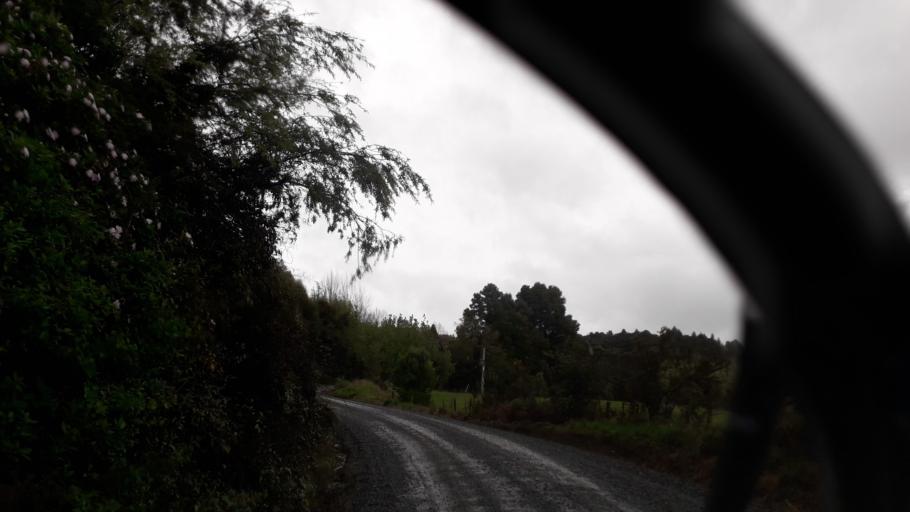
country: NZ
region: Northland
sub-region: Far North District
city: Kerikeri
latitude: -35.1195
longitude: 173.7517
